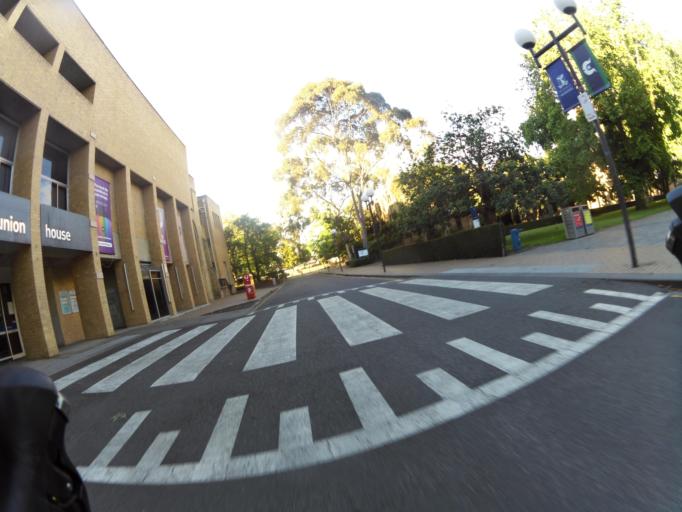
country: AU
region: Victoria
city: Carlton
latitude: -37.7970
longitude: 144.9615
